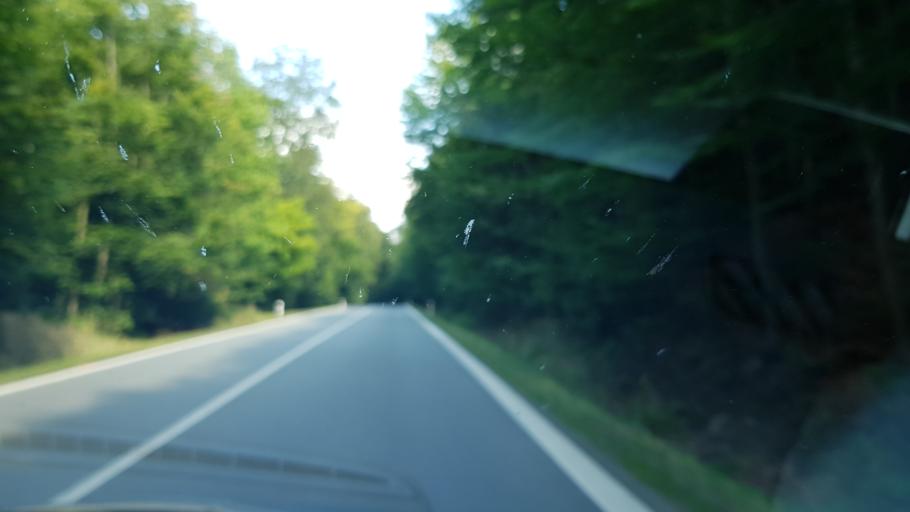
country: CZ
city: Vamberk
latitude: 50.1222
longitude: 16.3367
